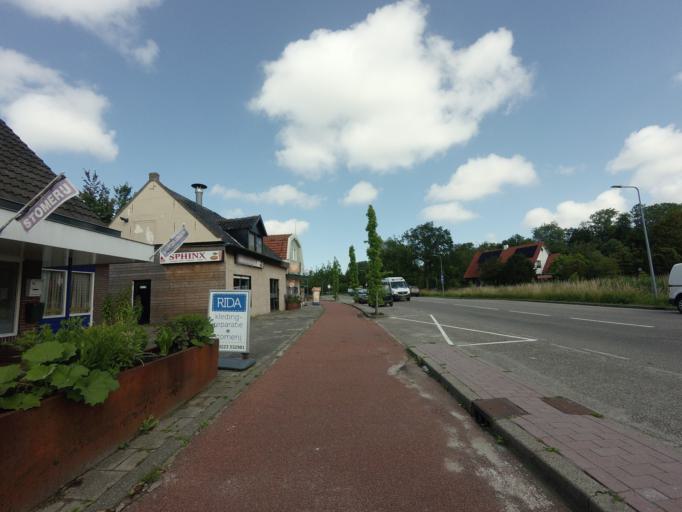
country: NL
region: North Holland
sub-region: Gemeente Schagen
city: Schagen
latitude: 52.8613
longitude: 4.8352
